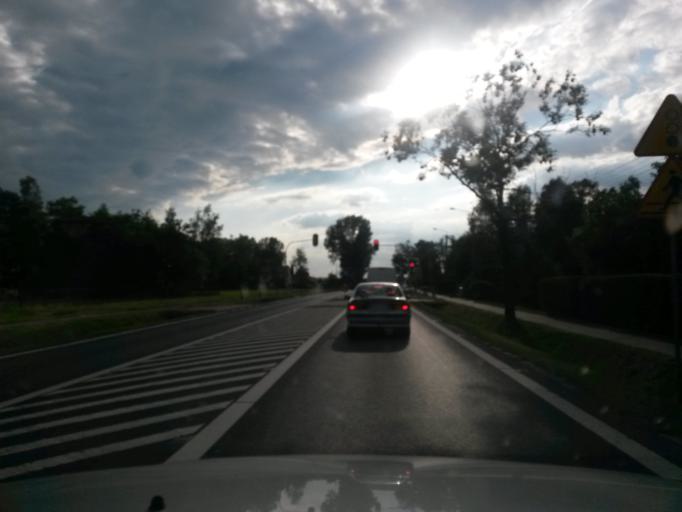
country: PL
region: Lodz Voivodeship
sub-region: Powiat piotrkowski
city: Grabica
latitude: 51.4158
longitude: 19.5626
